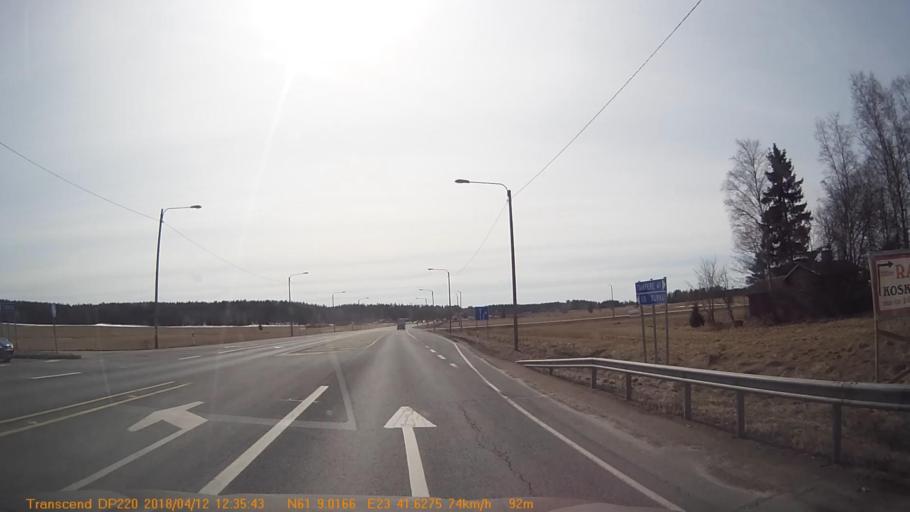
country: FI
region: Pirkanmaa
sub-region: Etelae-Pirkanmaa
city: Kylmaekoski
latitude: 61.1504
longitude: 23.6938
